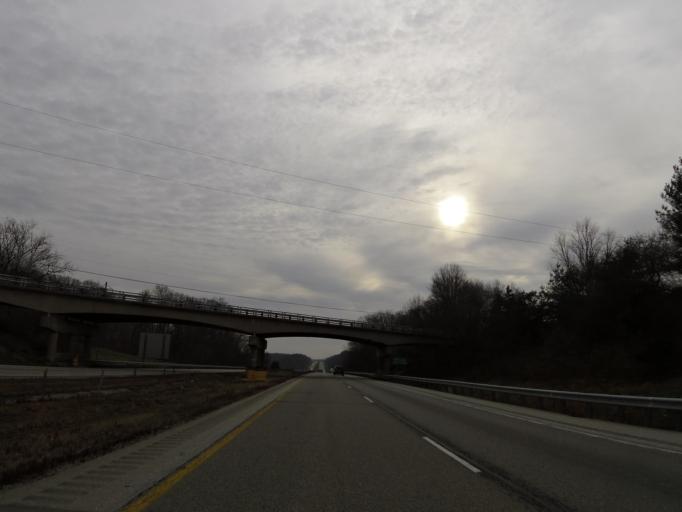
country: US
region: Illinois
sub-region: Vermilion County
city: Catlin
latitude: 40.1177
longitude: -87.6985
